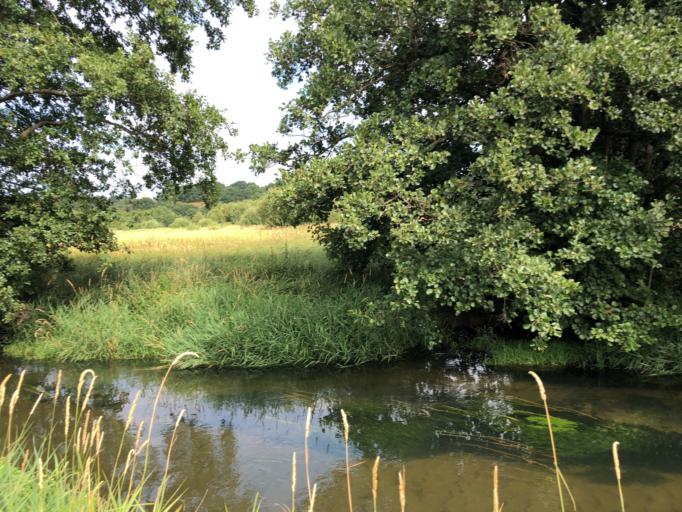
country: DK
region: South Denmark
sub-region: Vejle Kommune
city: Egtved
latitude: 55.6511
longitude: 9.2811
